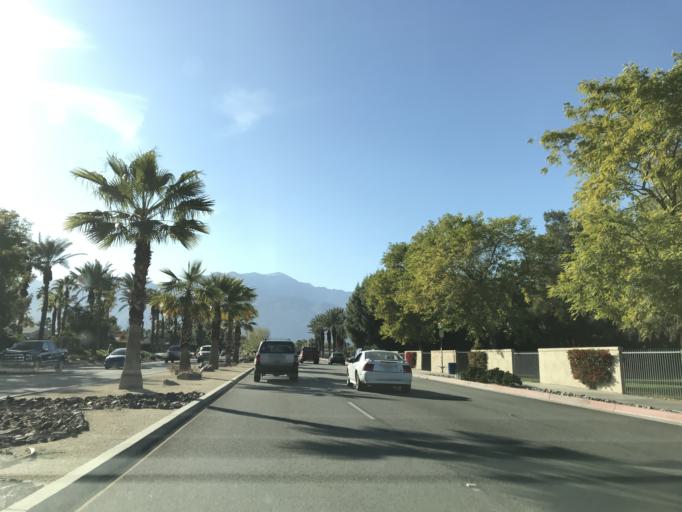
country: US
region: California
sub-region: Riverside County
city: Cathedral City
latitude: 33.8160
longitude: -116.4421
